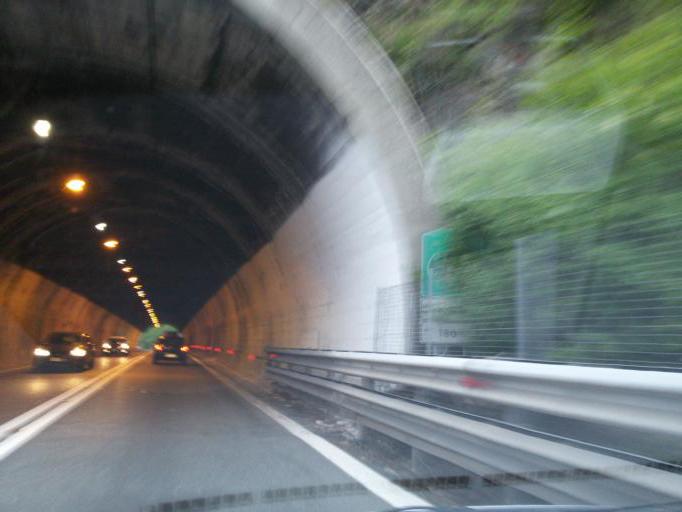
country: IT
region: Liguria
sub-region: Provincia di Genova
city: Genoa
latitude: 44.4359
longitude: 8.9420
